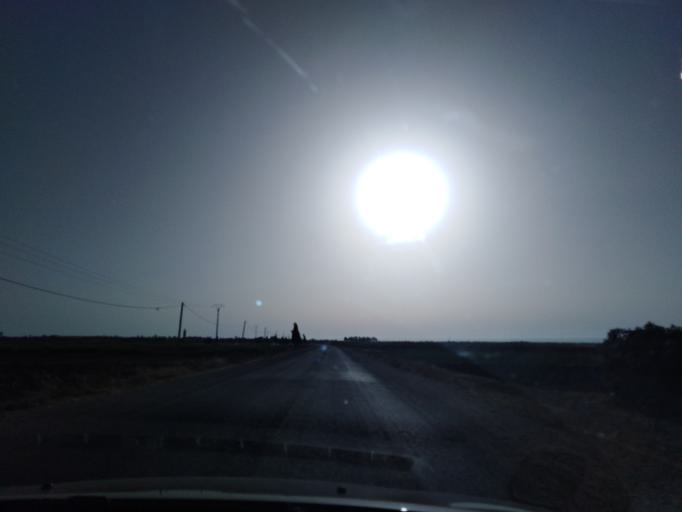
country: MA
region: Doukkala-Abda
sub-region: Safi
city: Safi
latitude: 32.4783
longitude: -8.8835
